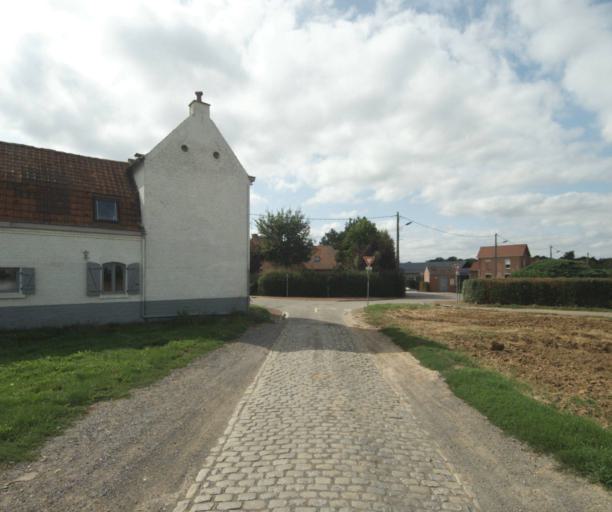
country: FR
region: Nord-Pas-de-Calais
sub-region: Departement du Nord
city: Gruson
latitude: 50.5930
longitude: 3.2145
